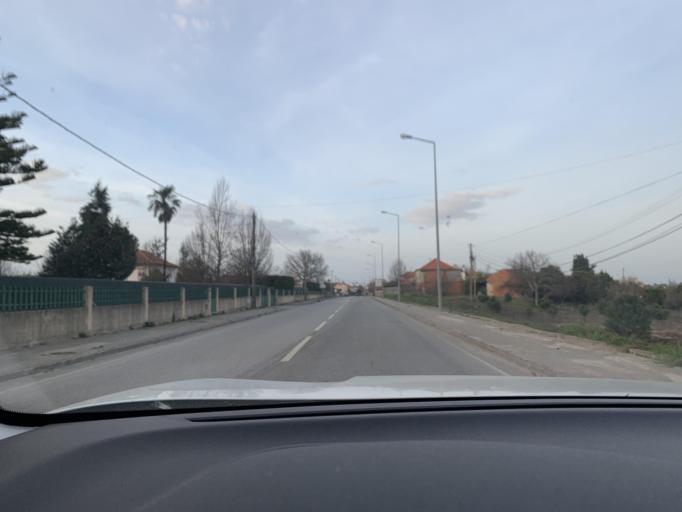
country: PT
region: Viseu
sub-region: Concelho de Tondela
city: Tondela
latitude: 40.4896
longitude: -8.0890
